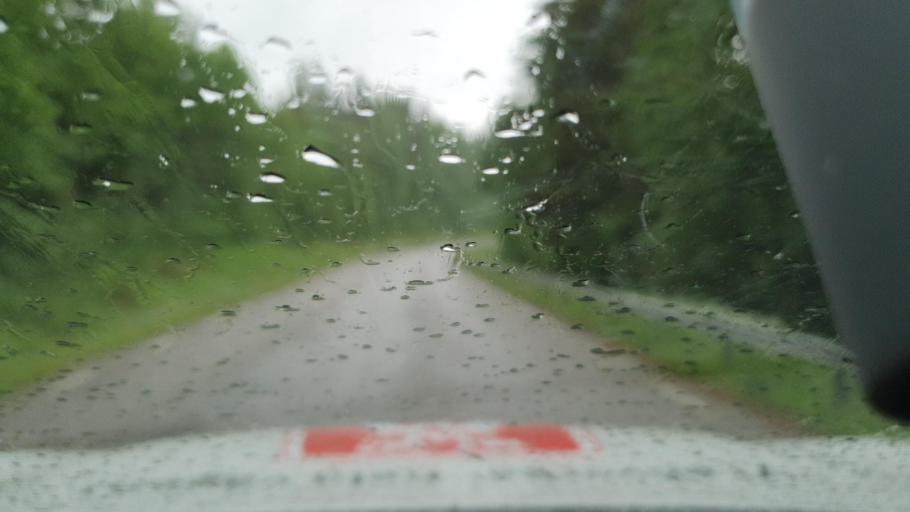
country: SE
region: Vaesterbotten
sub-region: Nordmalings Kommun
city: Nordmaling
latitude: 63.7897
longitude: 19.5606
